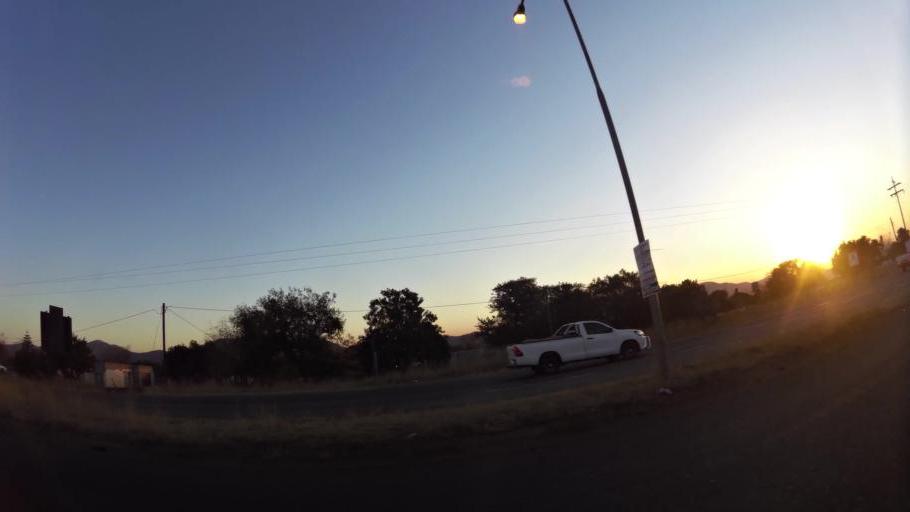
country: ZA
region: North-West
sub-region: Bojanala Platinum District Municipality
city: Rustenburg
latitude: -25.6111
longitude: 27.1770
